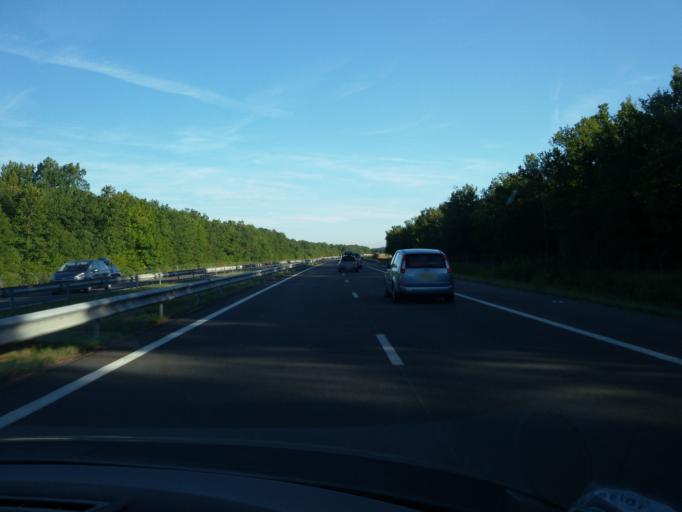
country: FR
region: Centre
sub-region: Departement du Cher
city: Levet
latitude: 46.8801
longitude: 2.4215
